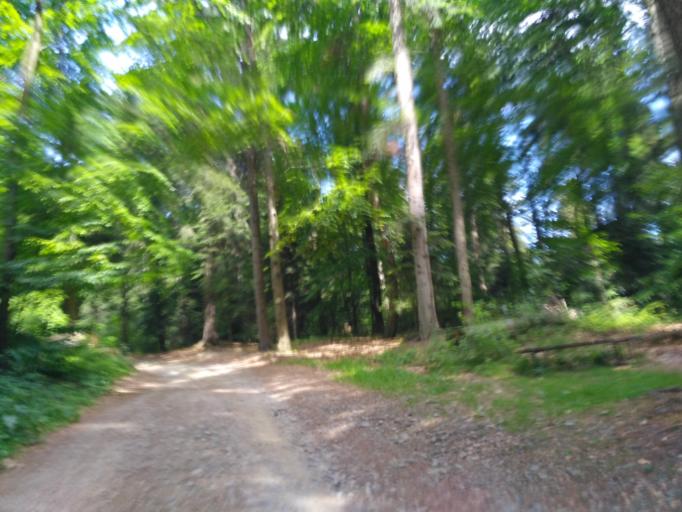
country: PL
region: Subcarpathian Voivodeship
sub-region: Powiat jasielski
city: Brzyska
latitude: 49.8075
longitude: 21.3629
